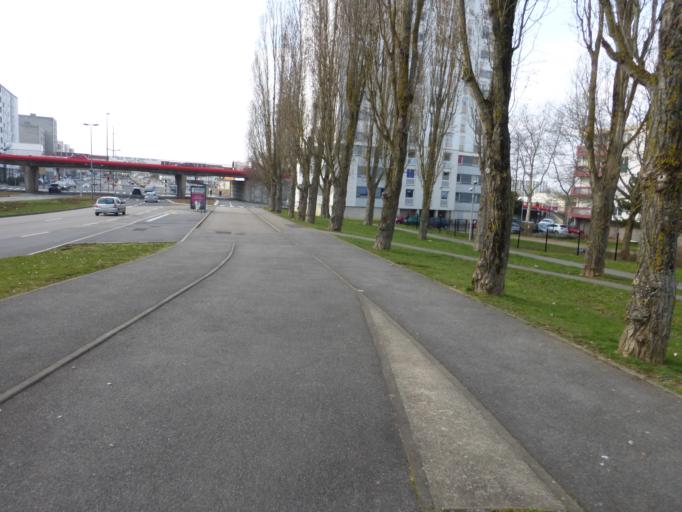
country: FR
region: Lorraine
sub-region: Departement de Meurthe-et-Moselle
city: Vandoeuvre-les-Nancy
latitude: 48.6601
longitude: 6.1767
